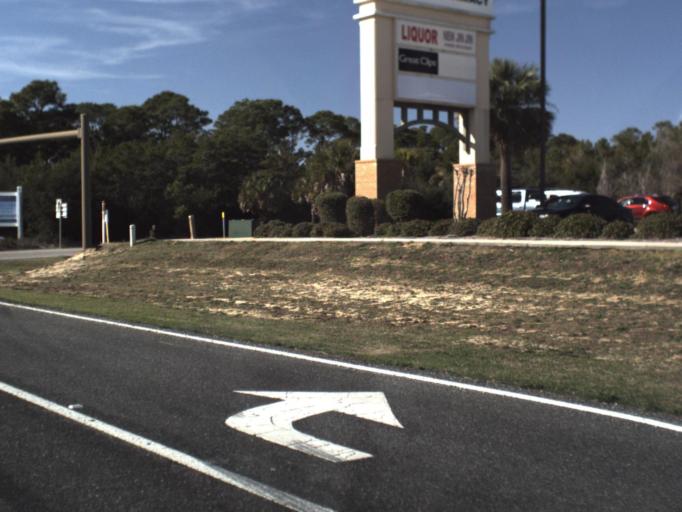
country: US
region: Florida
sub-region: Bay County
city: Laguna Beach
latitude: 30.2649
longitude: -85.9745
